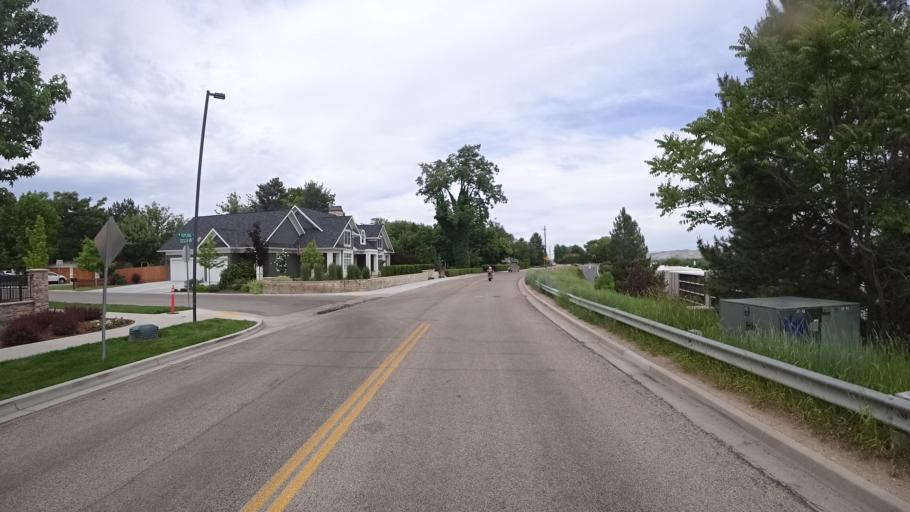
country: US
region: Idaho
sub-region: Ada County
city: Boise
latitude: 43.6050
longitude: -116.2195
